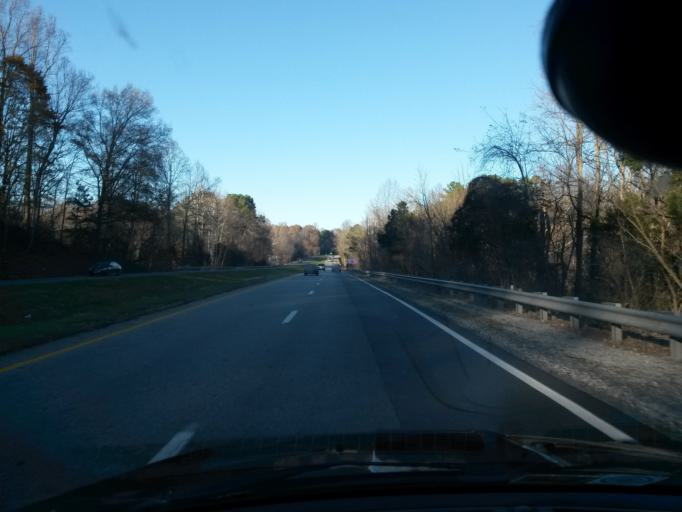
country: US
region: Virginia
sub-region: Amherst County
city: Amherst
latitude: 37.5705
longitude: -79.0530
